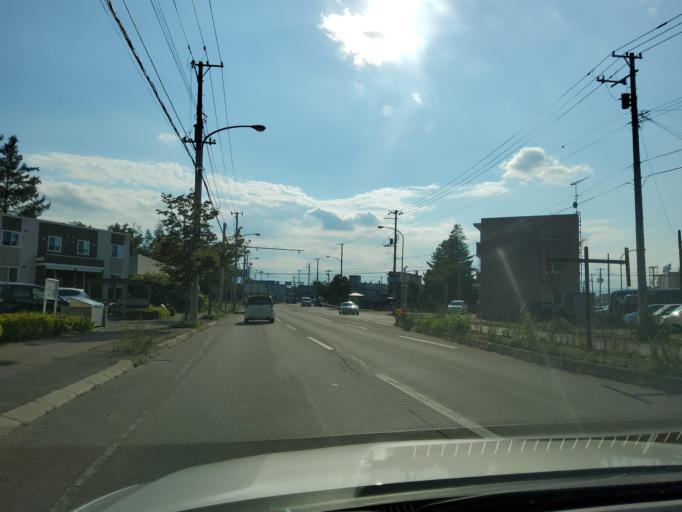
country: JP
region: Hokkaido
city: Obihiro
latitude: 42.9007
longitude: 143.2107
